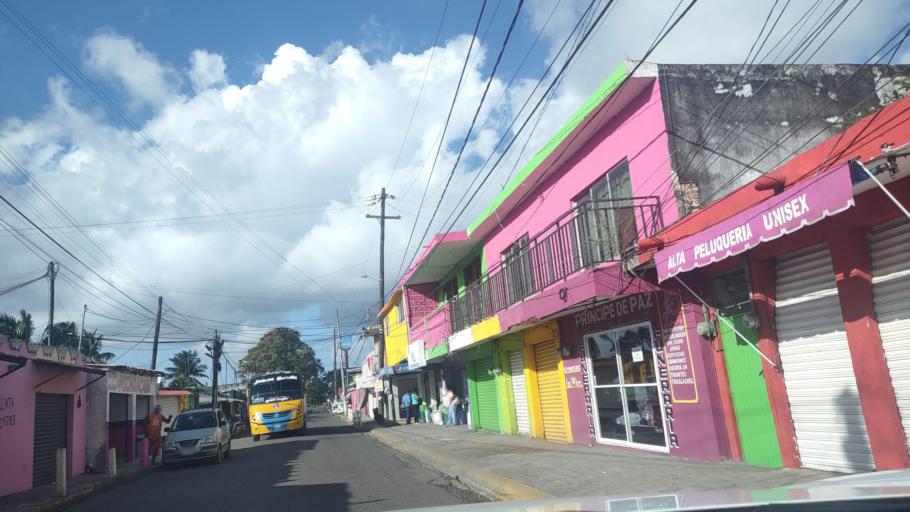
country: MX
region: Veracruz
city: El Tejar
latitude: 19.0703
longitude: -96.1614
